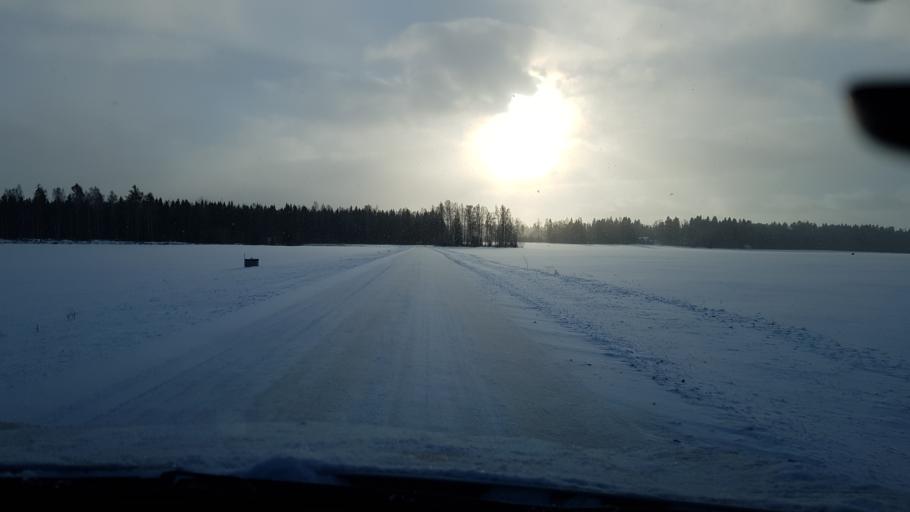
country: EE
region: Harju
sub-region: Nissi vald
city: Turba
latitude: 59.2018
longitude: 24.1399
